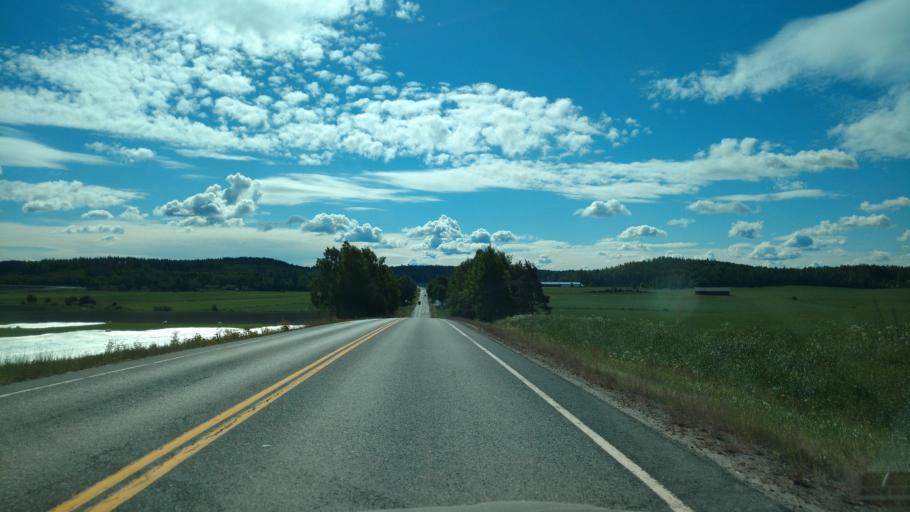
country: FI
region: Varsinais-Suomi
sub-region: Salo
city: Muurla
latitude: 60.3809
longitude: 23.2966
